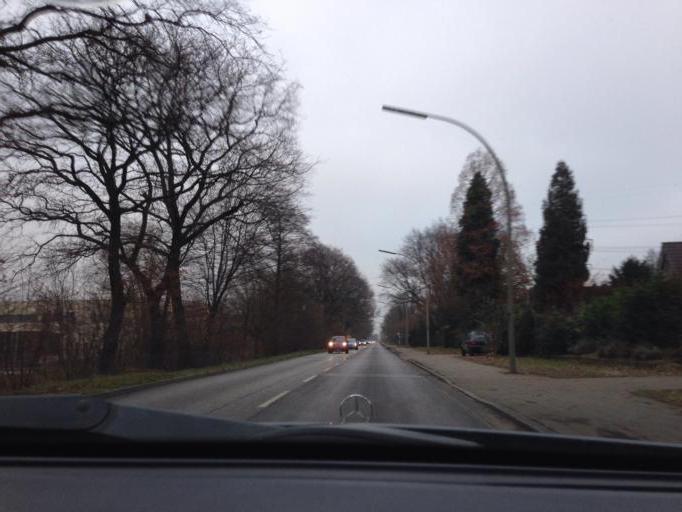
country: DE
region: Schleswig-Holstein
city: Stapelfeld
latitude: 53.6312
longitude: 10.1829
